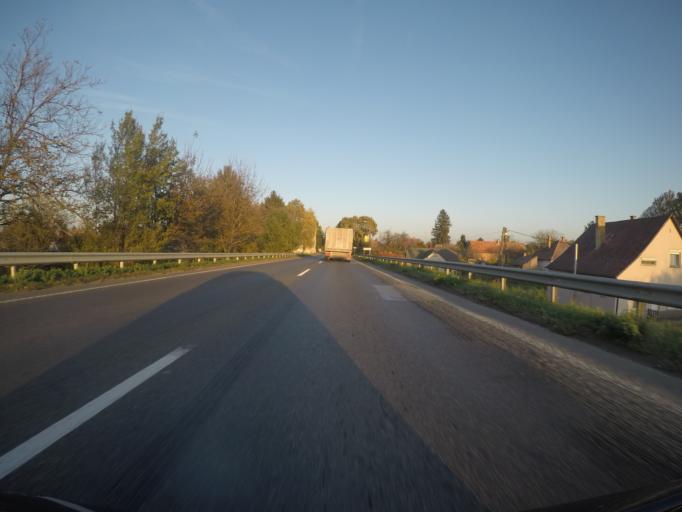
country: HU
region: Baranya
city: Szentlorinc
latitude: 46.0443
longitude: 17.9809
